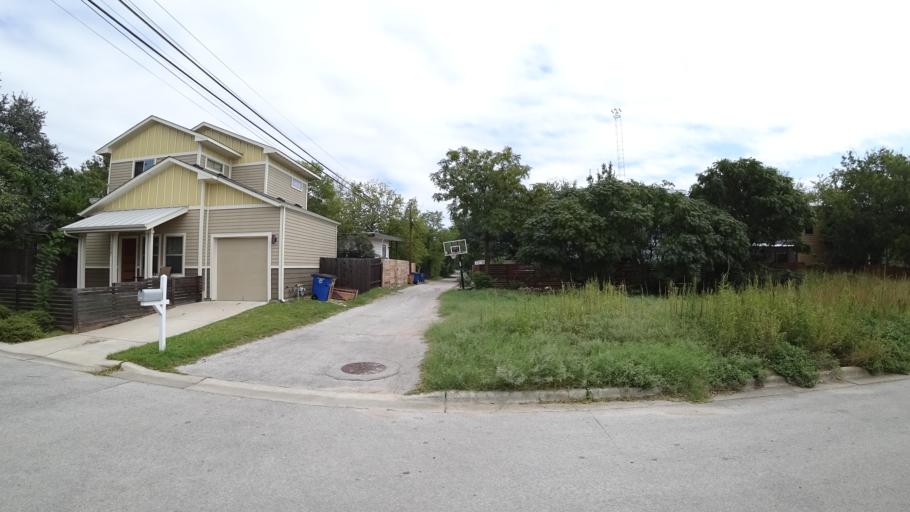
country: US
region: Texas
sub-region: Travis County
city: Austin
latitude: 30.2756
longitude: -97.7183
